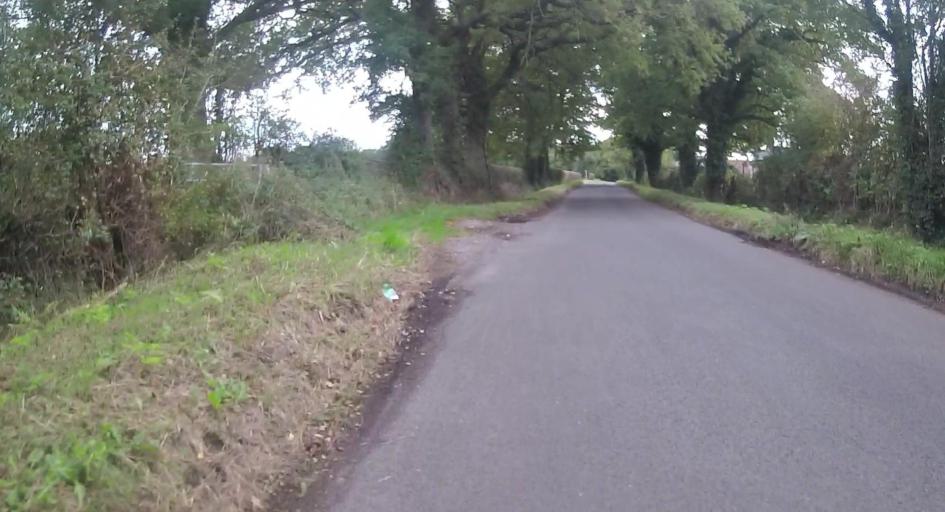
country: GB
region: England
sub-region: Hampshire
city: Fleet
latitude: 51.2834
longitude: -0.8884
